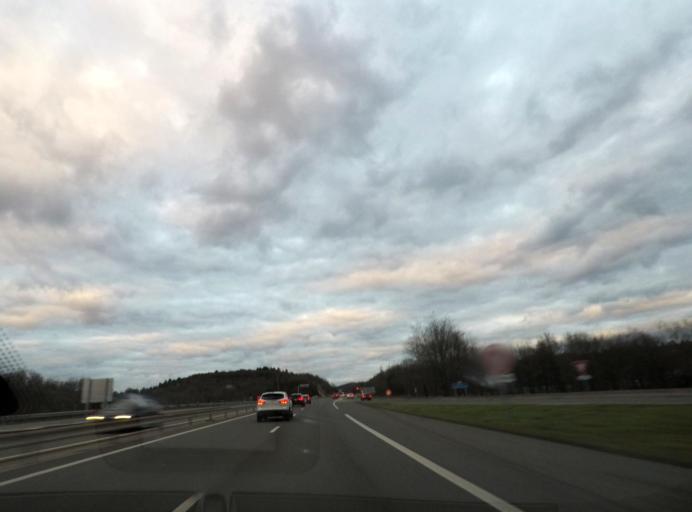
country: FR
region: Rhone-Alpes
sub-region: Departement de l'Ain
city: Saint-Martin-du-Frene
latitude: 46.1189
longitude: 5.4933
